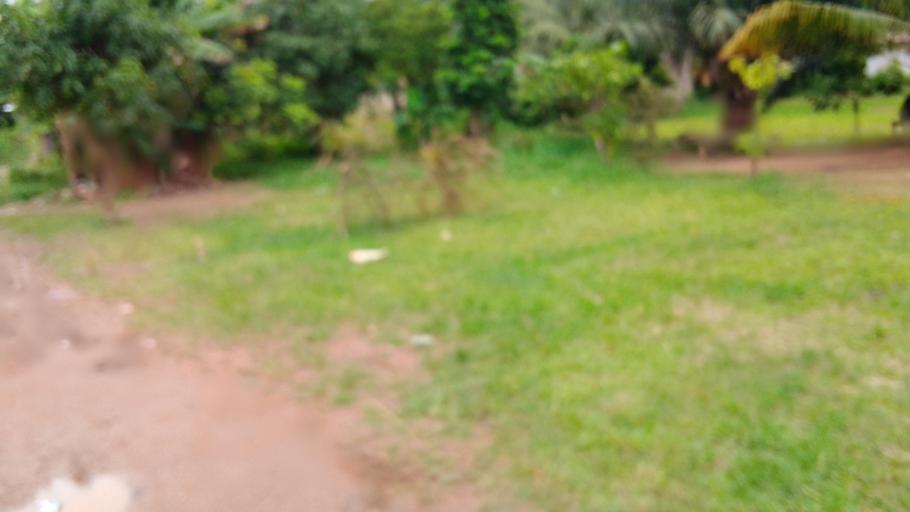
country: SL
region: Eastern Province
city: Kenema
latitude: 7.8551
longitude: -11.1885
